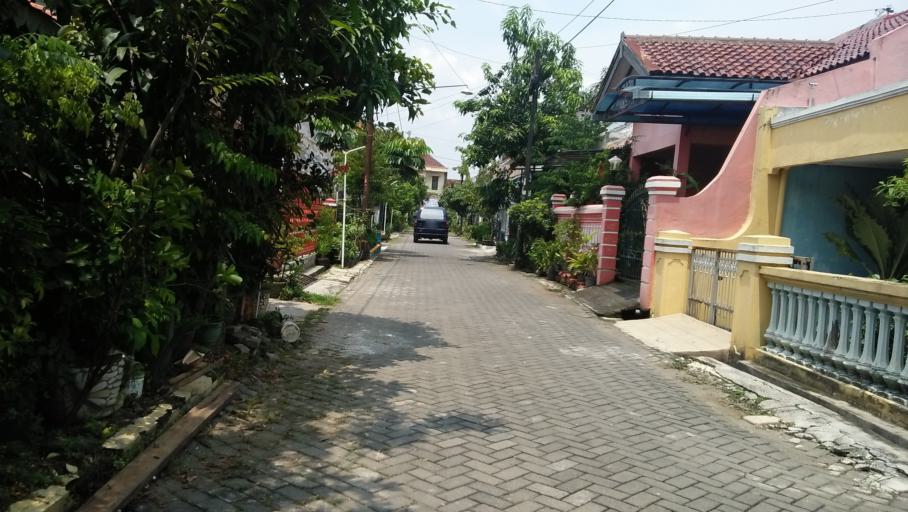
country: ID
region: Central Java
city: Mranggen
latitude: -7.0312
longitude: 110.4639
